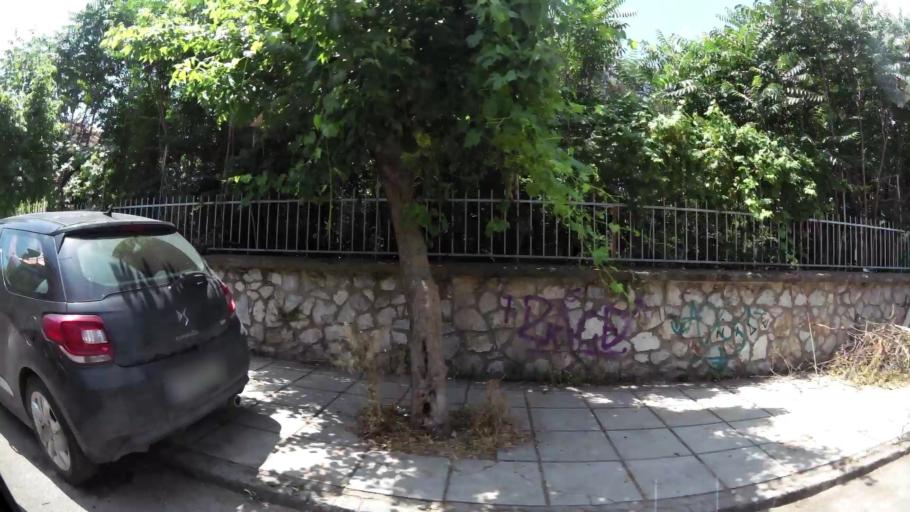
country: GR
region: Central Macedonia
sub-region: Nomos Thessalonikis
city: Triandria
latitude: 40.6129
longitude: 22.9759
